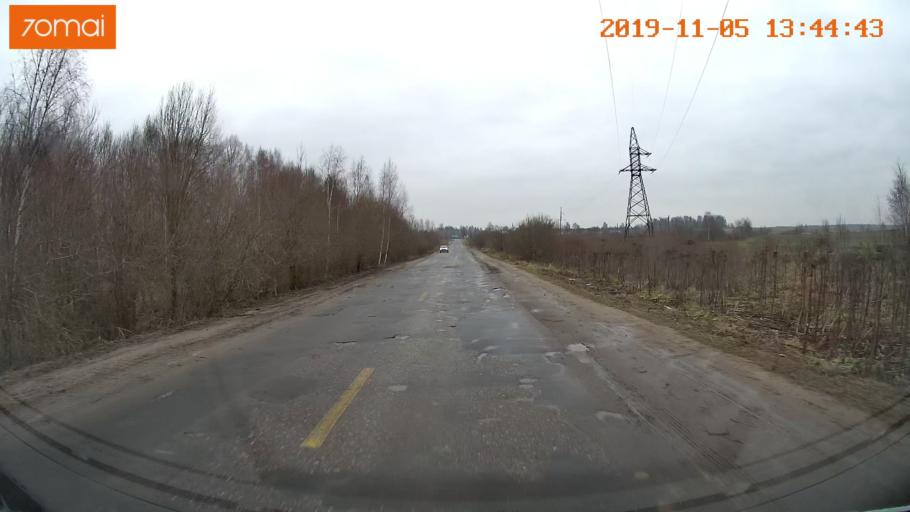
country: RU
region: Ivanovo
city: Shuya
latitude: 56.9830
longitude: 41.4113
